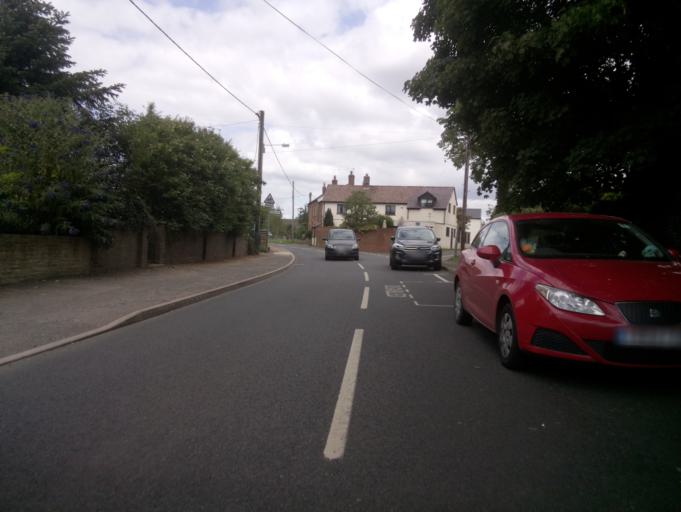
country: GB
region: England
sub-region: Buckinghamshire
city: Newton Longville
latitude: 51.9523
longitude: -0.8134
